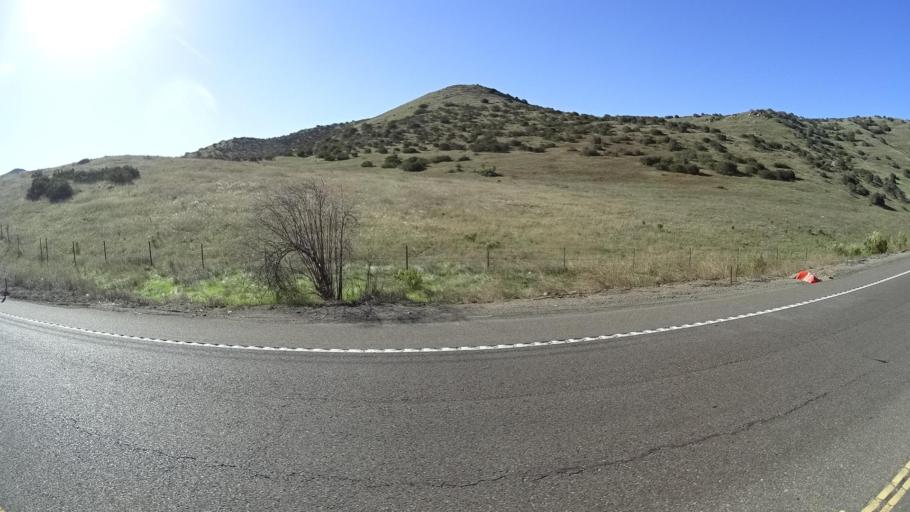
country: US
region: California
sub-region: San Diego County
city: Jamul
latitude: 32.6643
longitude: -116.8167
